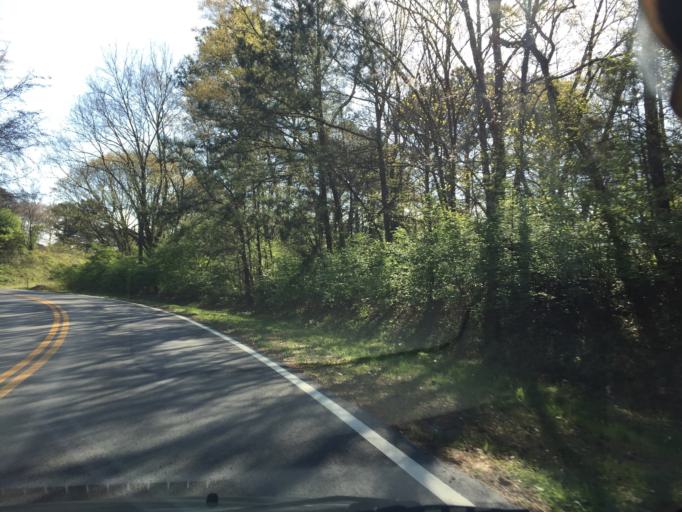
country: US
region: Tennessee
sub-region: Hamilton County
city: East Chattanooga
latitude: 35.0679
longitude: -85.2120
